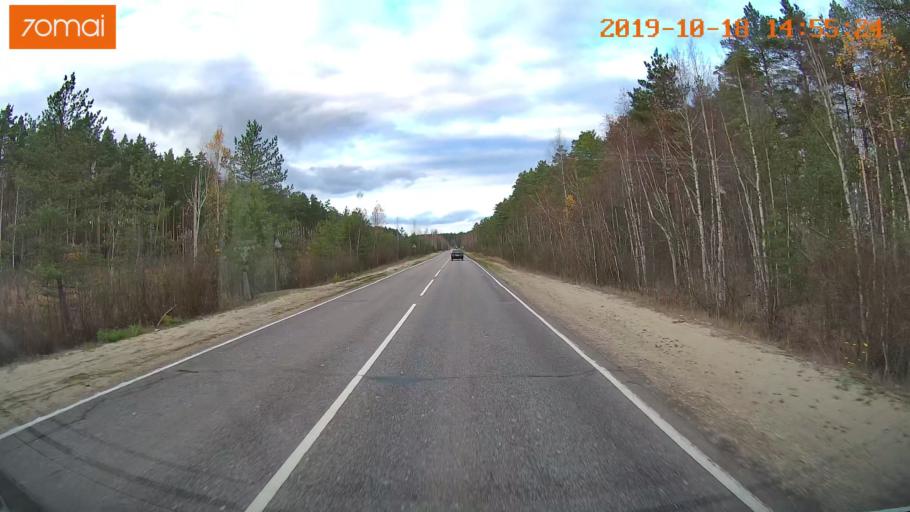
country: RU
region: Vladimir
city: Kurlovo
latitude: 55.4514
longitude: 40.5885
